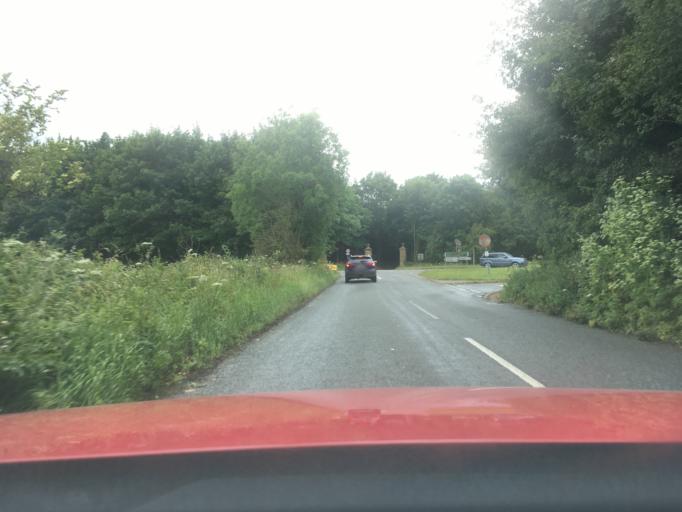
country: GB
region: England
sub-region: Worcestershire
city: Broadway
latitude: 52.0299
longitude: -1.8257
